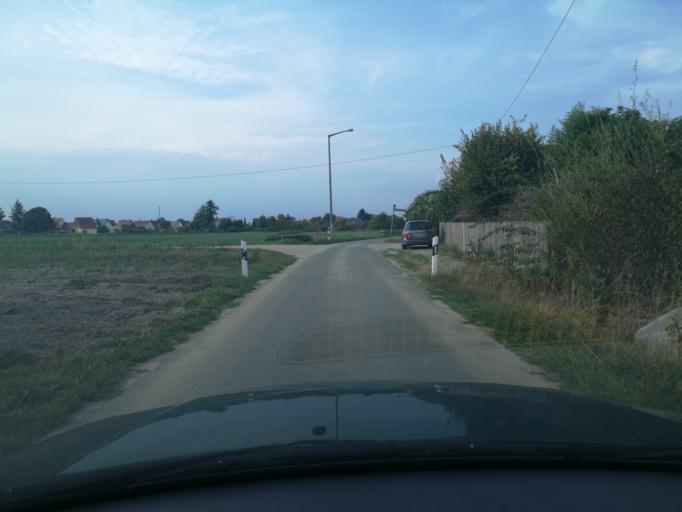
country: DE
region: Bavaria
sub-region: Regierungsbezirk Mittelfranken
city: Wetzendorf
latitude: 49.4850
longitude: 11.0644
